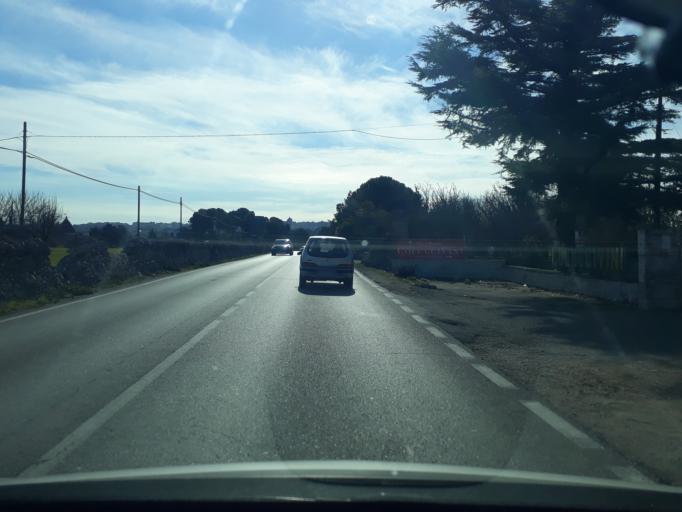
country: IT
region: Apulia
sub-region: Provincia di Taranto
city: Martina Franca
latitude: 40.7266
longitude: 17.3326
